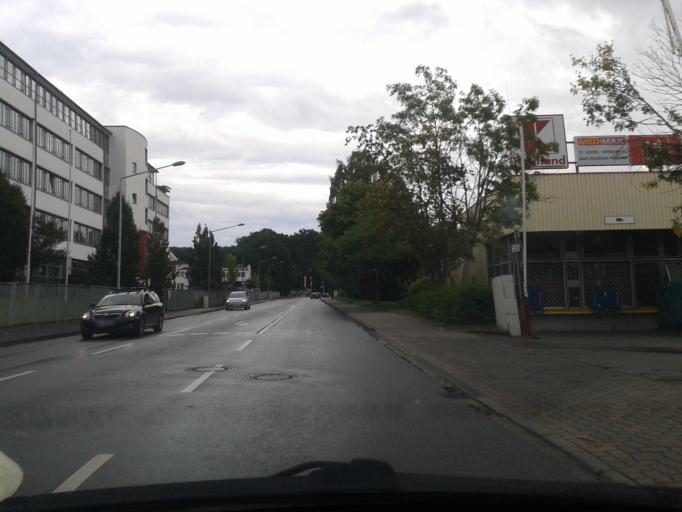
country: DE
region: North Rhine-Westphalia
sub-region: Regierungsbezirk Detmold
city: Detmold
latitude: 51.9536
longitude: 8.8854
